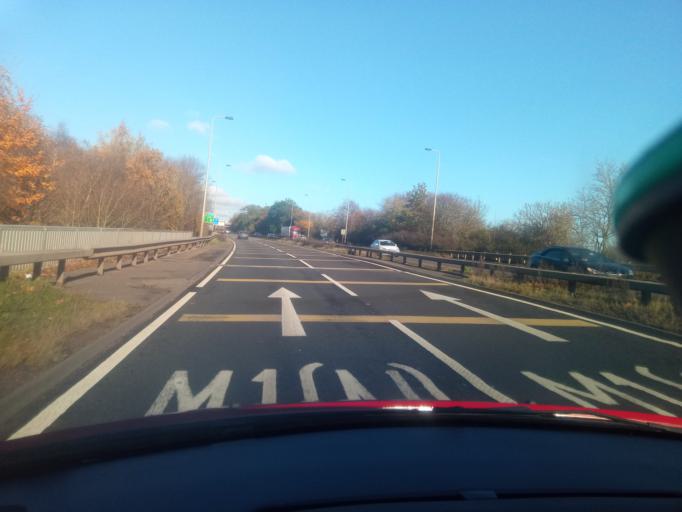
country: GB
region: England
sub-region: Derbyshire
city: Pinxton
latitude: 53.0971
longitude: -1.3270
